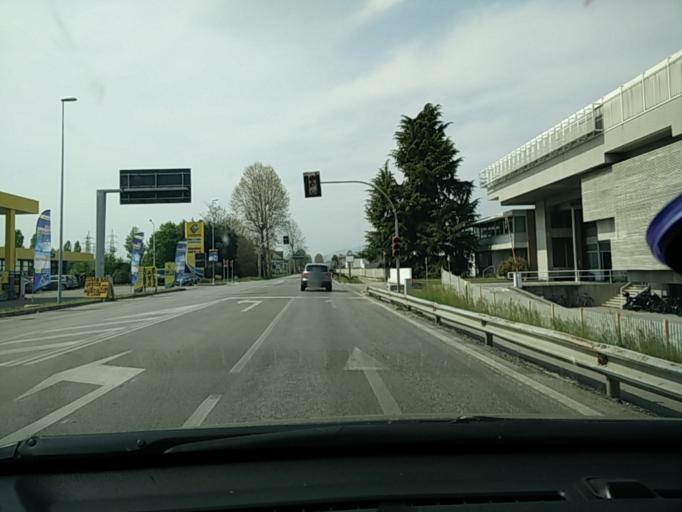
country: IT
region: Friuli Venezia Giulia
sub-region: Provincia di Pordenone
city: Porcia
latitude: 45.9679
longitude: 12.6244
